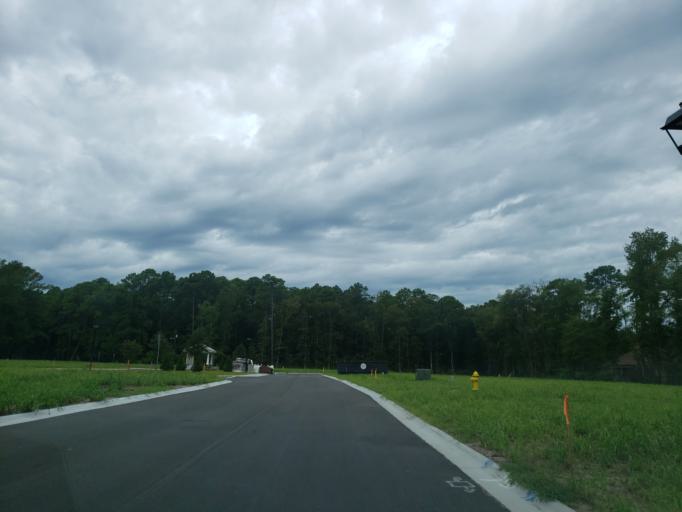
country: US
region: Georgia
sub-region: Chatham County
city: Isle of Hope
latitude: 32.0039
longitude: -81.0688
